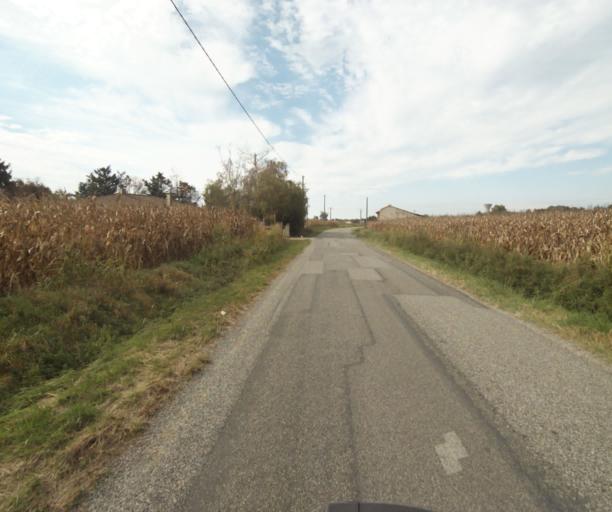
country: FR
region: Midi-Pyrenees
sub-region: Departement du Tarn-et-Garonne
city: Finhan
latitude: 43.9158
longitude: 1.2343
